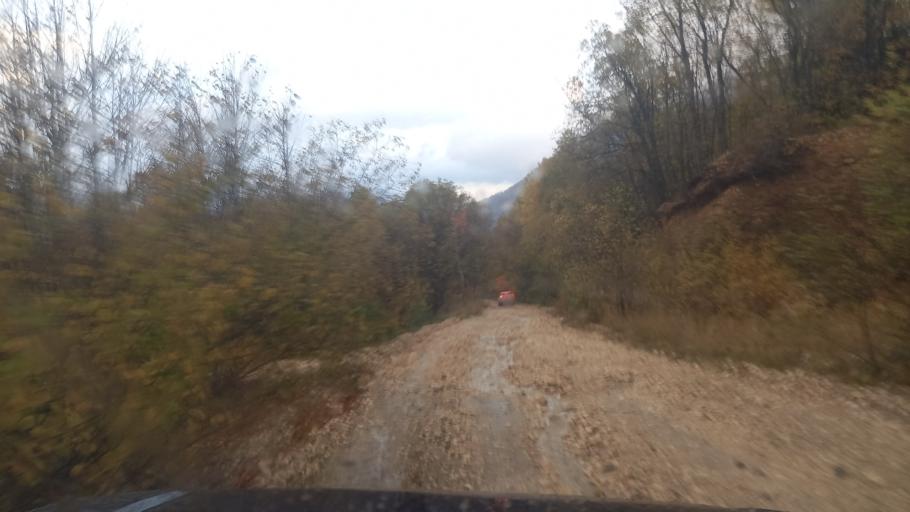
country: RU
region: Krasnodarskiy
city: Neftegorsk
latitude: 44.0228
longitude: 39.8386
